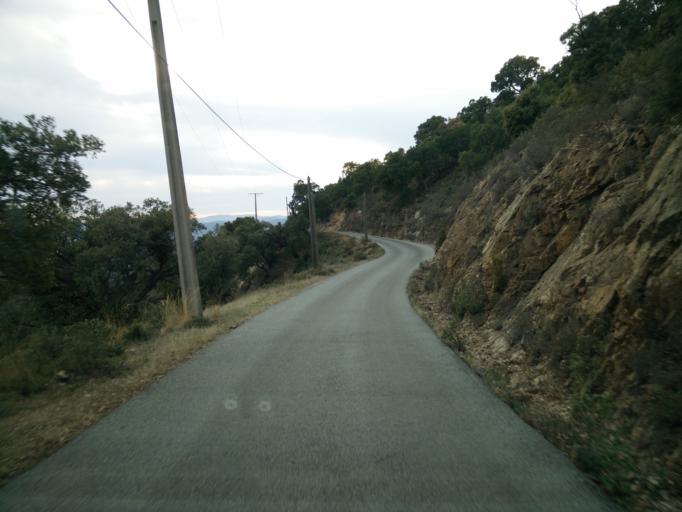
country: FR
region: Provence-Alpes-Cote d'Azur
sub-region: Departement du Var
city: Sainte-Maxime
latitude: 43.3642
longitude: 6.6119
